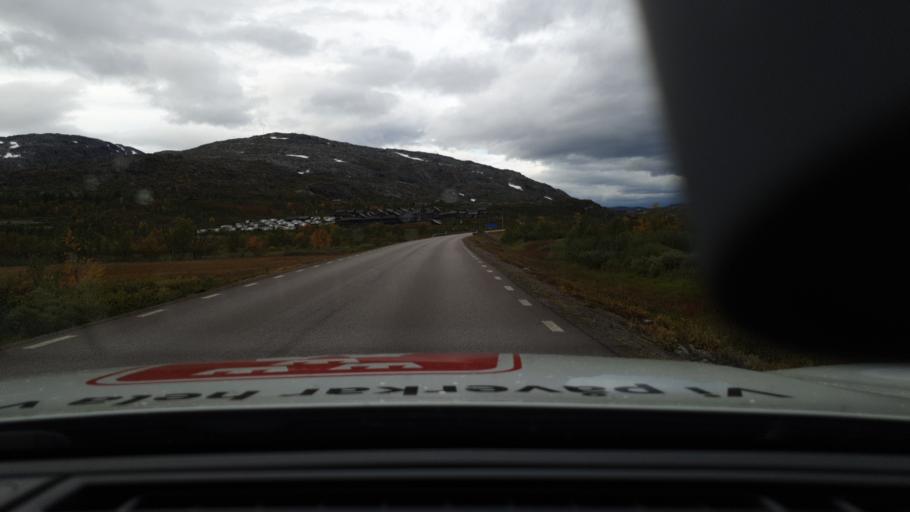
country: NO
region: Troms
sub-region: Bardu
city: Setermoen
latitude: 68.4260
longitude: 18.1740
